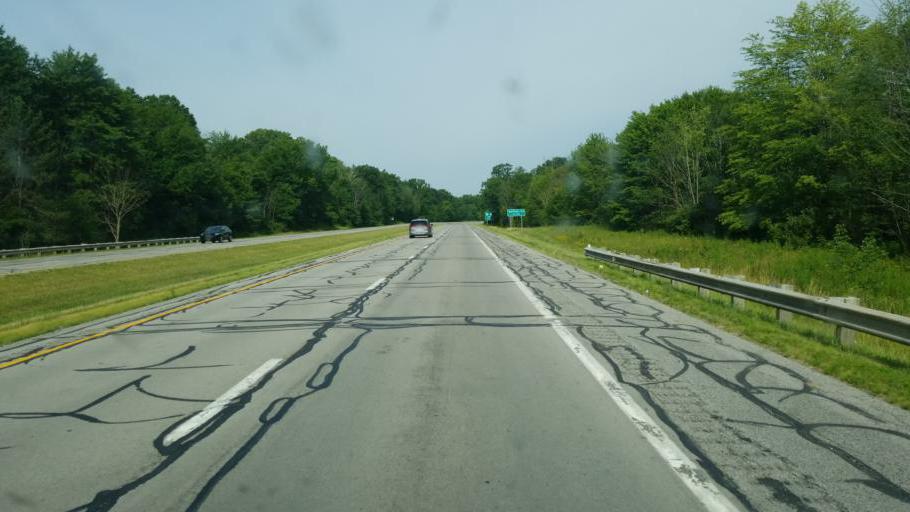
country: US
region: Ohio
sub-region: Medina County
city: Westfield Center
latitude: 41.0386
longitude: -81.9714
